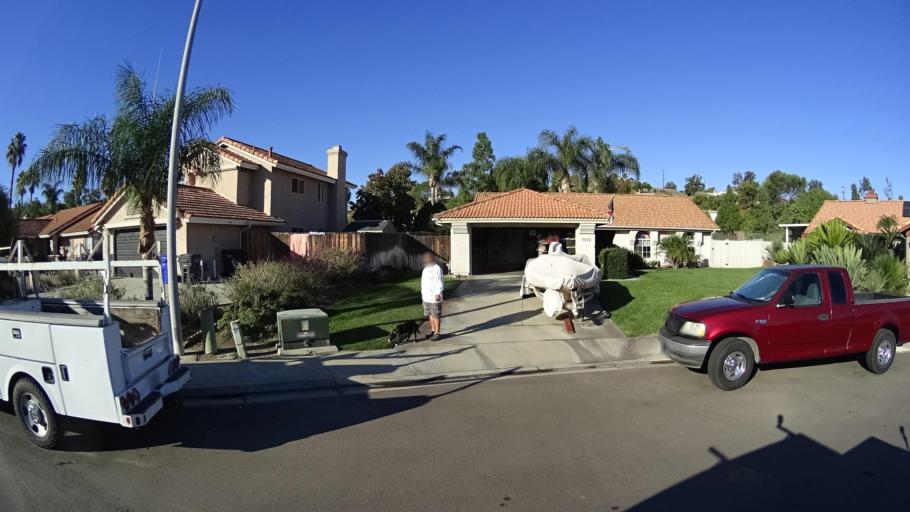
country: US
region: California
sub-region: San Diego County
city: Lakeside
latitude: 32.8530
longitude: -116.9202
